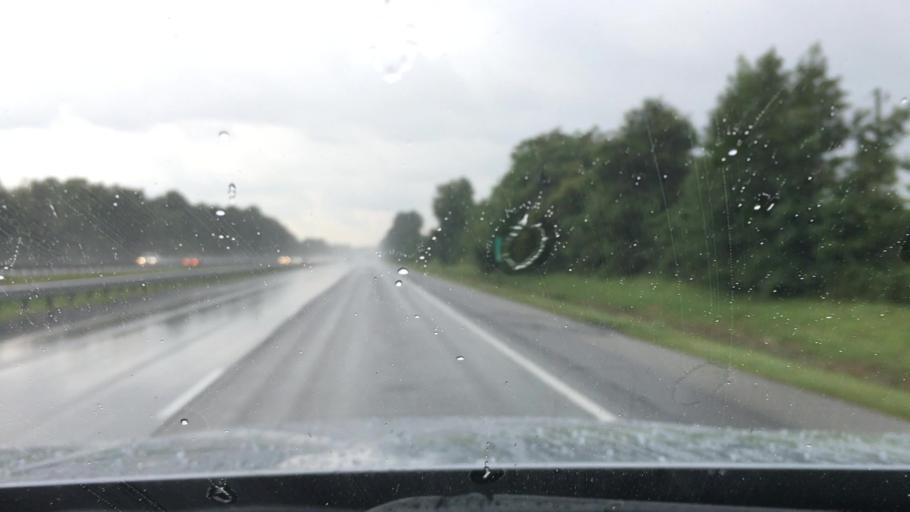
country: US
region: North Carolina
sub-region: Northampton County
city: Gaston
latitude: 36.5003
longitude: -77.5975
